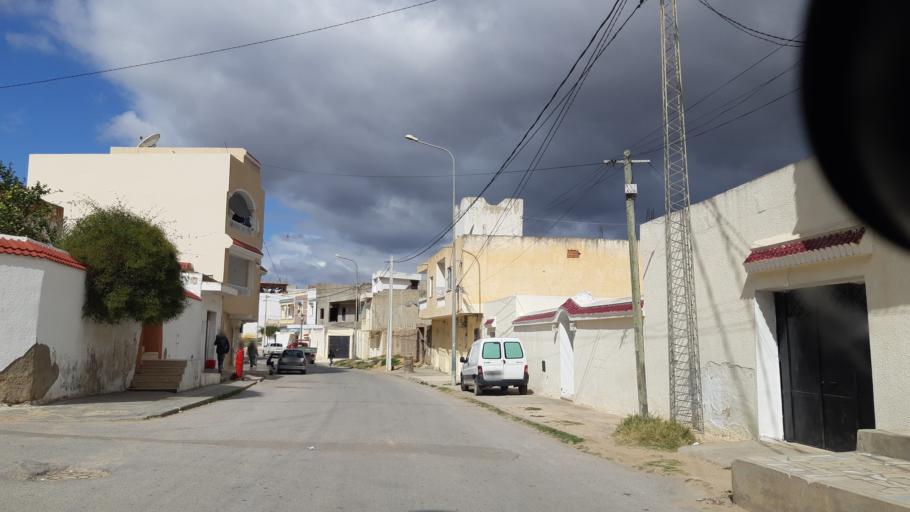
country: TN
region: Susah
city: Akouda
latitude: 35.8724
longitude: 10.5230
